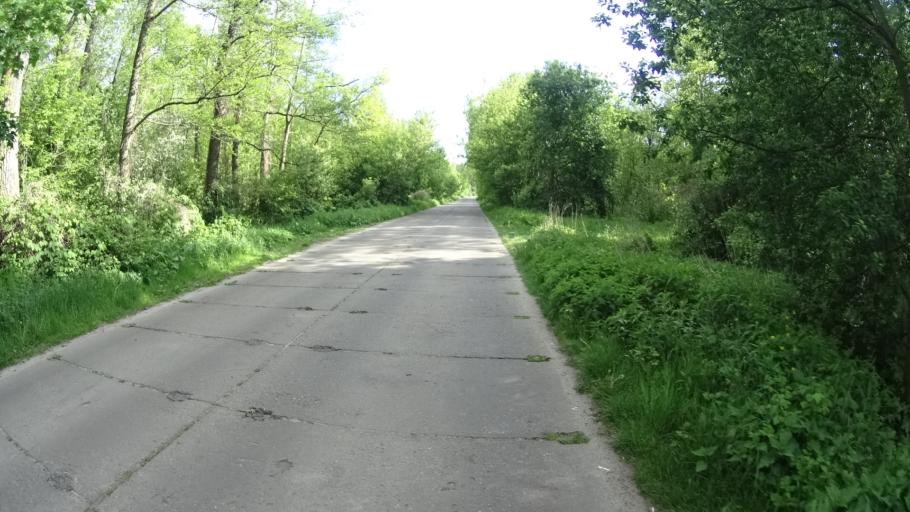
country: PL
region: Masovian Voivodeship
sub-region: Warszawa
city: Bemowo
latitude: 52.2824
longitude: 20.8864
